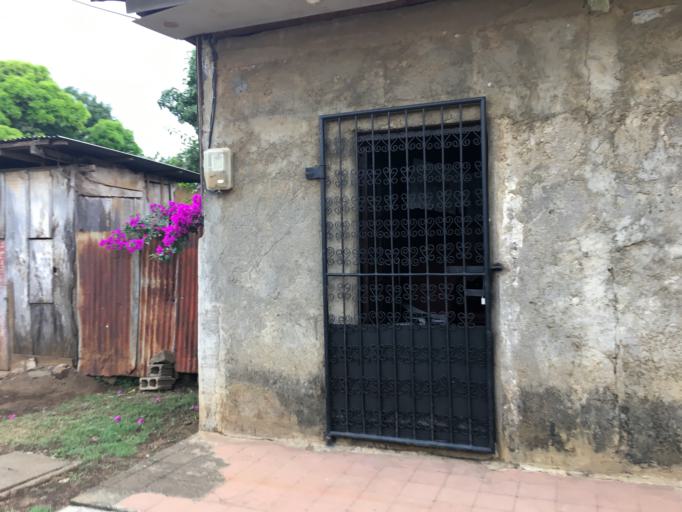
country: NI
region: Masaya
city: Masaya
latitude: 11.9824
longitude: -86.0935
